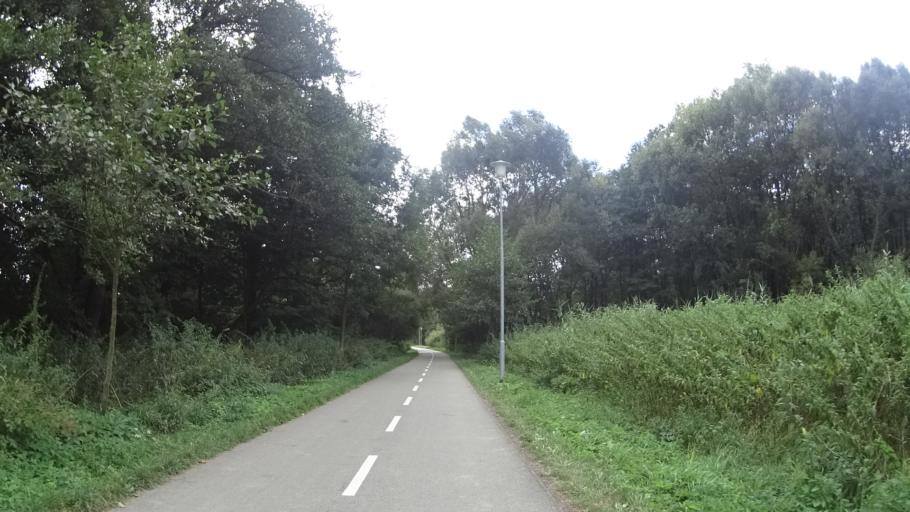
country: CZ
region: Pardubicky
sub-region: Okres Usti nad Orlici
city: Usti nad Orlici
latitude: 49.9786
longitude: 16.3862
